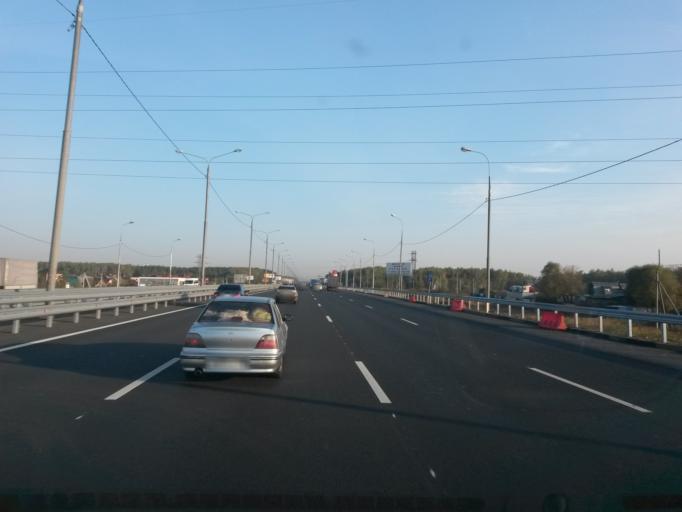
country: RU
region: Moskovskaya
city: Shcherbinka
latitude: 55.4830
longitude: 37.6142
